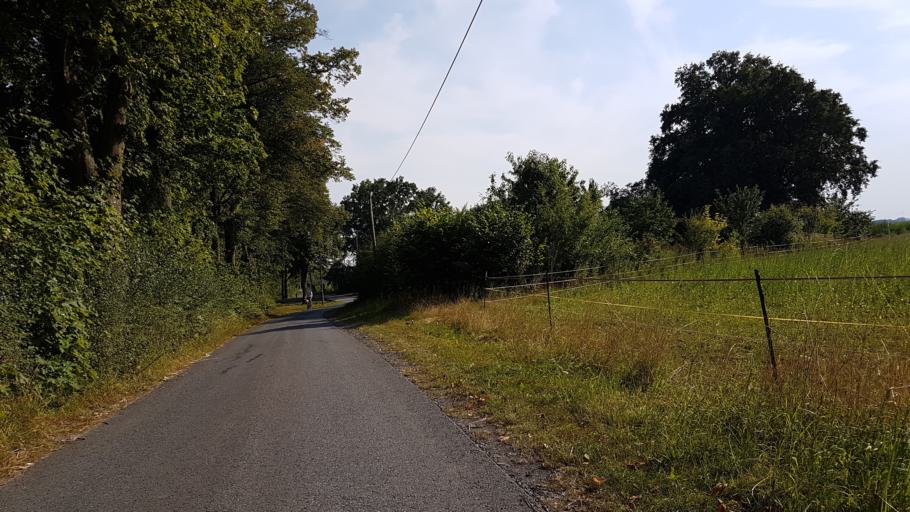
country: DE
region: North Rhine-Westphalia
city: Olfen
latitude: 51.6872
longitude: 7.3768
